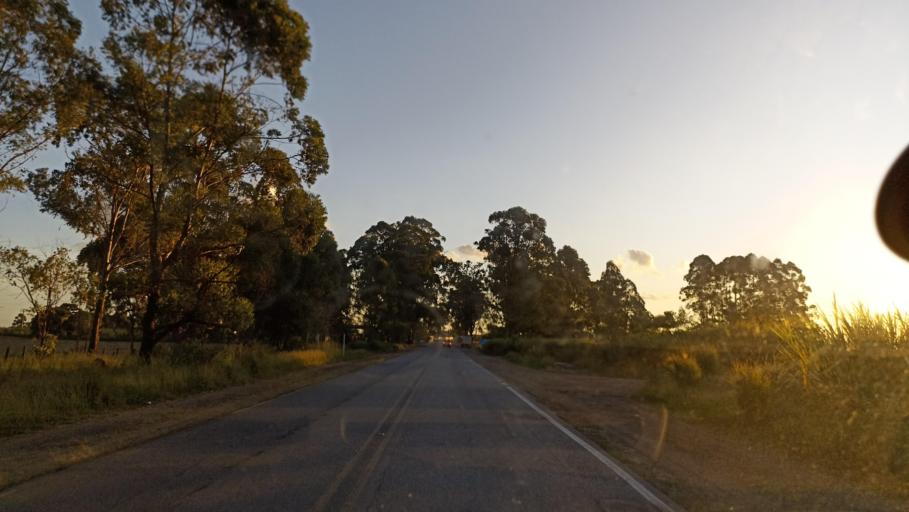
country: BR
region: Minas Gerais
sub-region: Sao Joao Del Rei
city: Sao Joao del Rei
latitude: -21.2400
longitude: -44.4001
